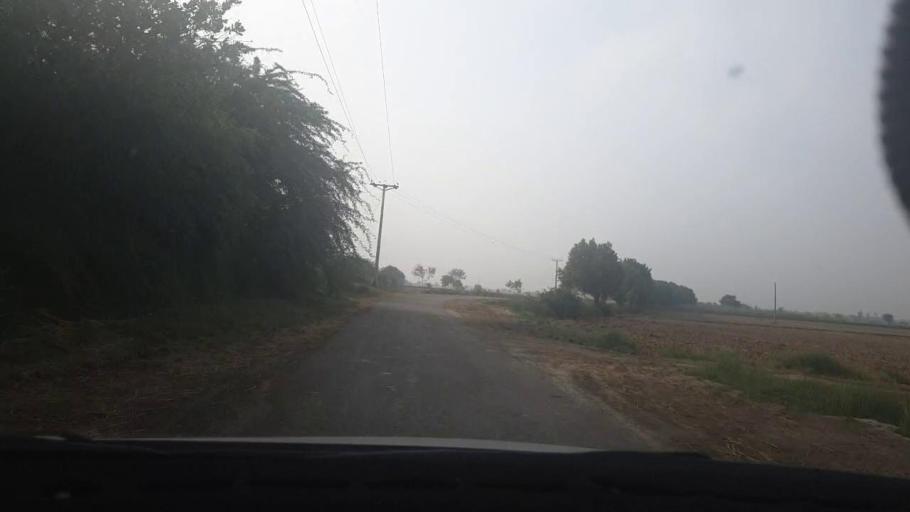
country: PK
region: Sindh
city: Tando Muhammad Khan
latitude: 25.0875
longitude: 68.5163
